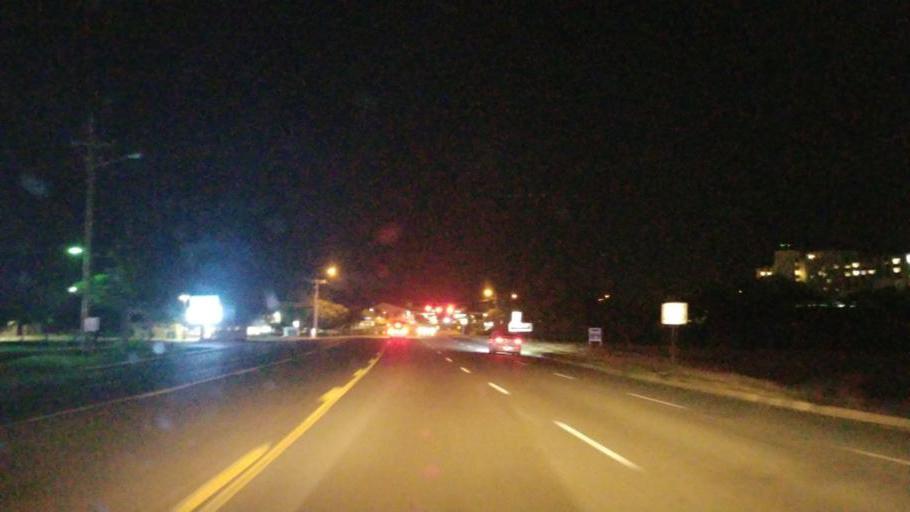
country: US
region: Texas
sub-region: Potter County
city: Amarillo
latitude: 35.1930
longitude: -101.9206
